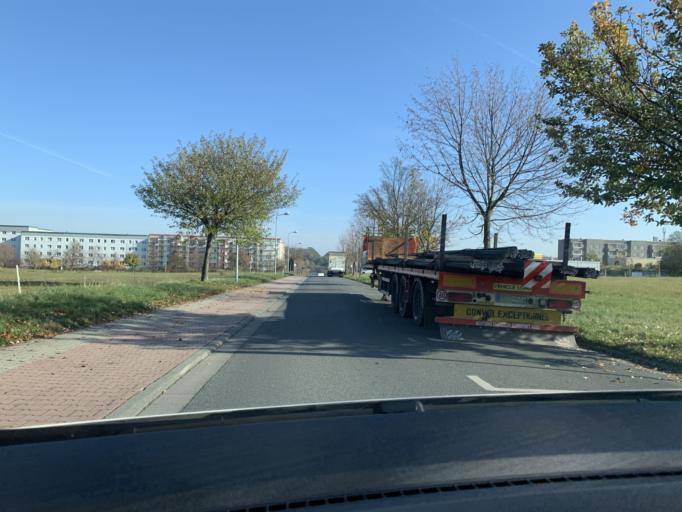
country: DE
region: Thuringia
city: Schmolln
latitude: 50.8851
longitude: 12.3485
